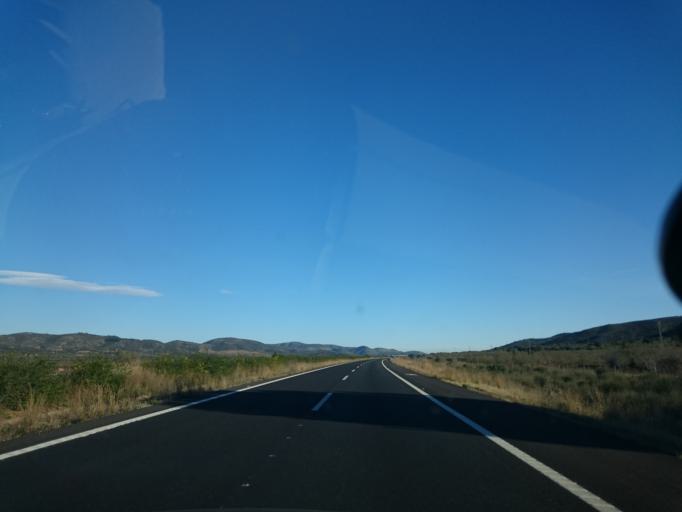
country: ES
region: Valencia
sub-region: Provincia de Castello
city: Alcala de Xivert
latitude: 40.3096
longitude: 0.2416
